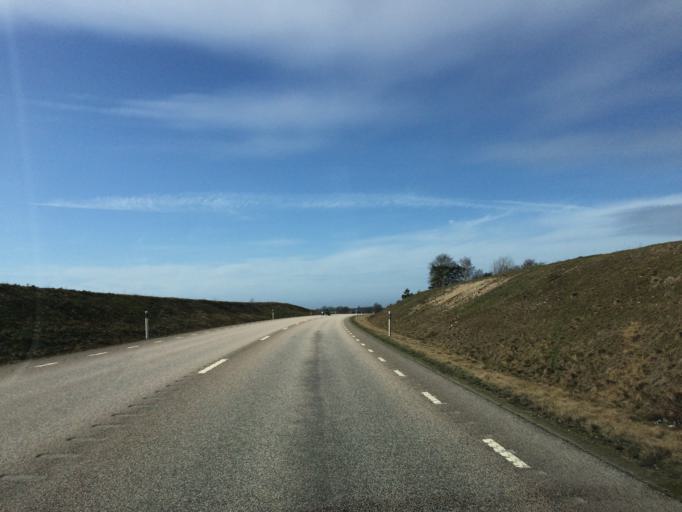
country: SE
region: Halland
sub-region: Laholms Kommun
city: Veinge
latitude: 56.5435
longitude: 13.0616
